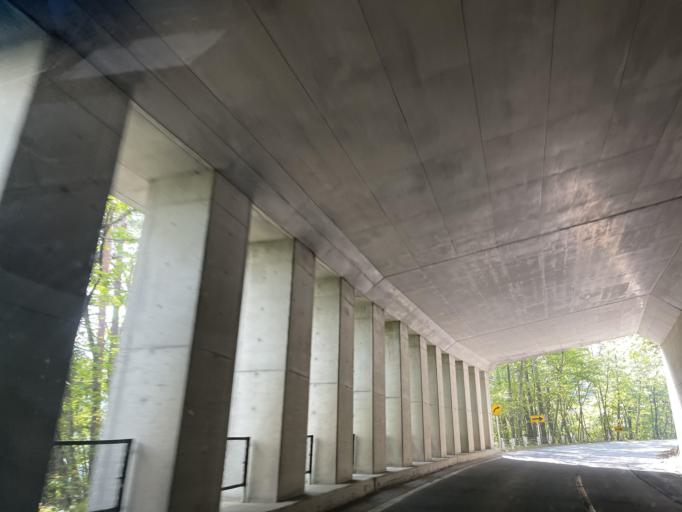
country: JP
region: Nagano
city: Omachi
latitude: 36.5224
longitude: 137.7903
